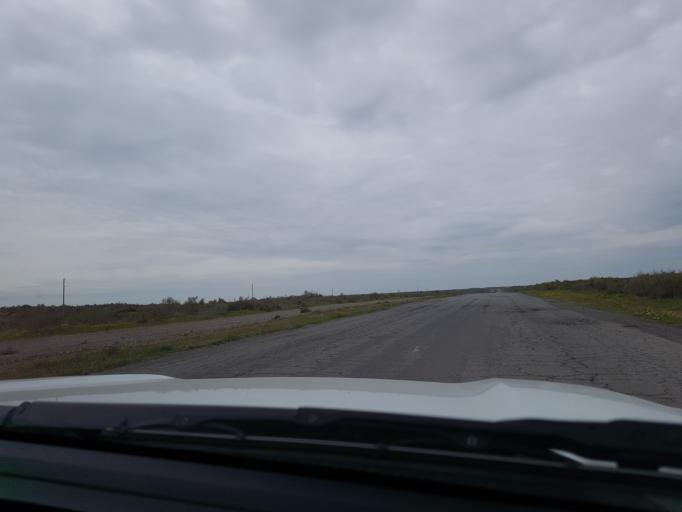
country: TM
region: Mary
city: Bayramaly
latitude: 37.9098
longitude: 62.6205
